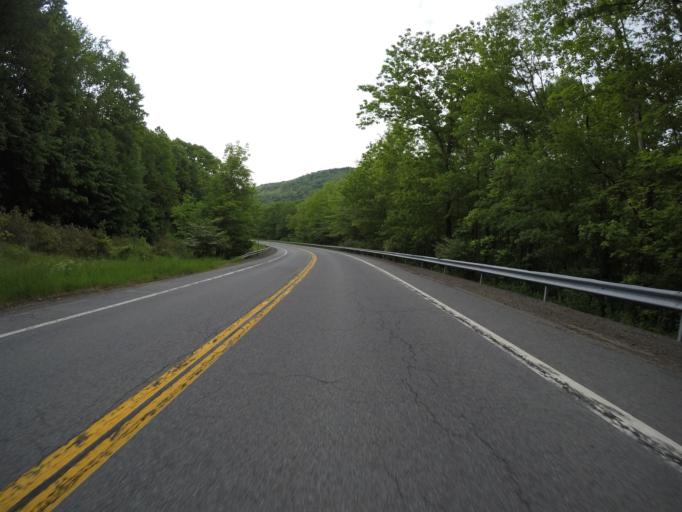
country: US
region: New York
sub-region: Sullivan County
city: Livingston Manor
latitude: 42.0752
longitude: -74.8352
